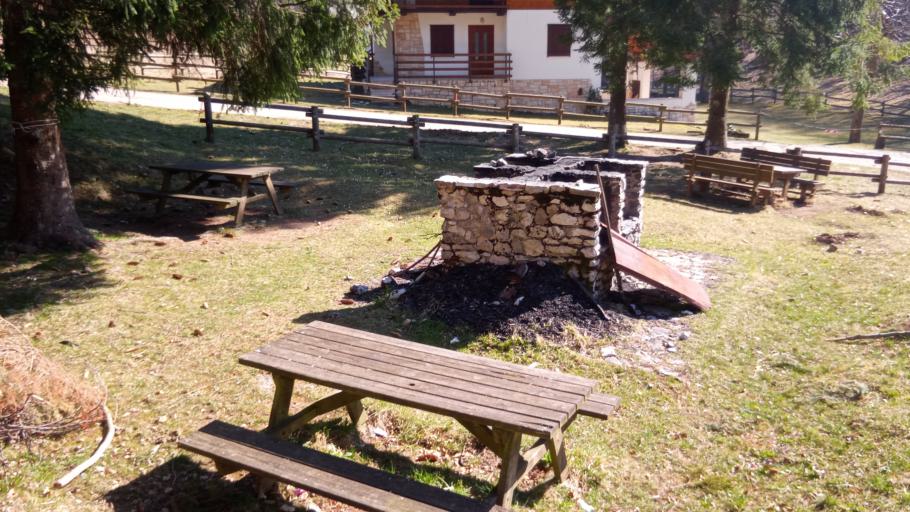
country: IT
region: Veneto
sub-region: Provincia di Treviso
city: Borso del Grappa
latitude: 45.8369
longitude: 11.7786
